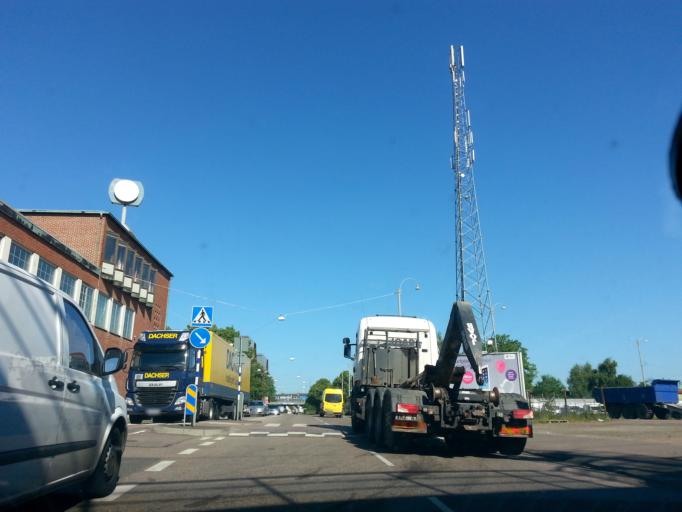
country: SE
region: Vaestra Goetaland
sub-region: Goteborg
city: Goeteborg
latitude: 57.7294
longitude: 12.0045
